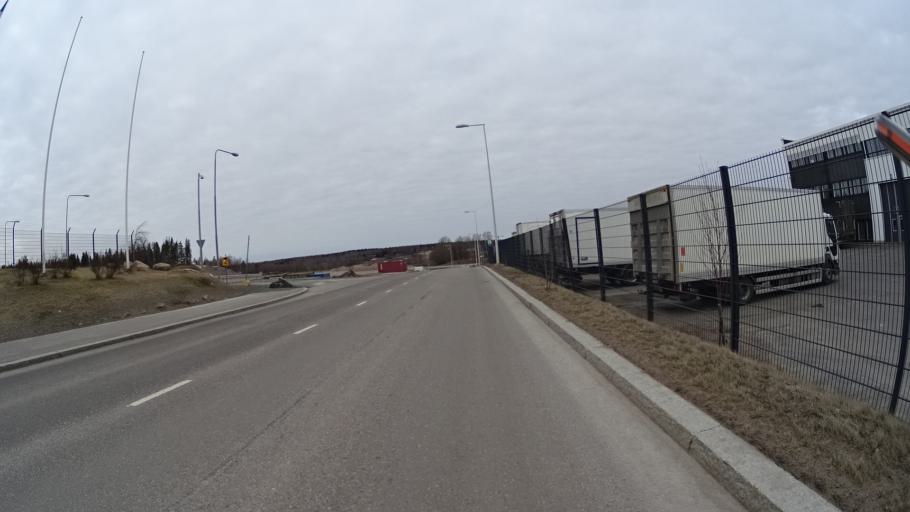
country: FI
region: Uusimaa
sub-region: Helsinki
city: Teekkarikylae
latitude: 60.3065
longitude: 24.8894
